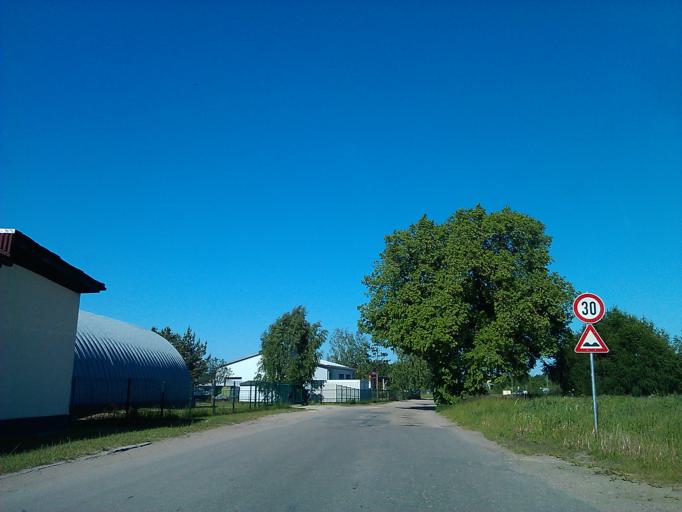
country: LV
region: Adazi
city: Adazi
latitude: 57.0969
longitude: 24.3179
